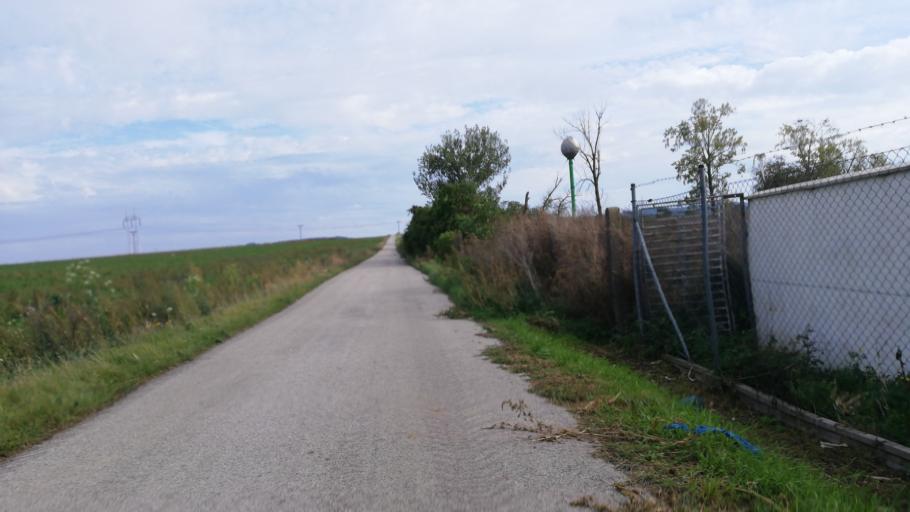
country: CZ
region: South Moravian
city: Sudomerice
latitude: 48.8500
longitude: 17.2537
